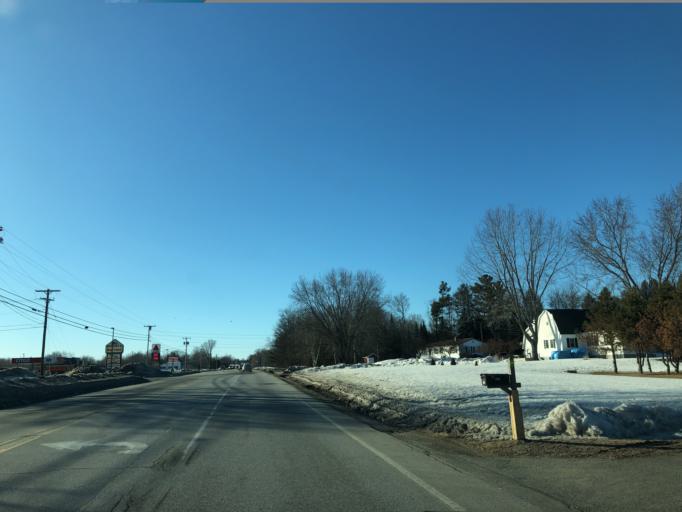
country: US
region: Maine
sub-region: Penobscot County
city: Kenduskeag
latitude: 44.9828
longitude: -69.0011
